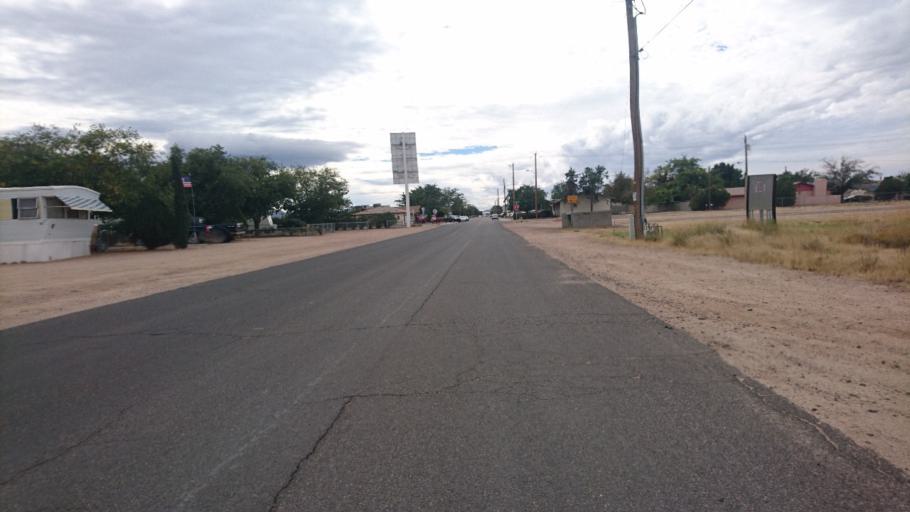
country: US
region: Arizona
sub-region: Mohave County
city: New Kingman-Butler
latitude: 35.2331
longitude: -114.0183
